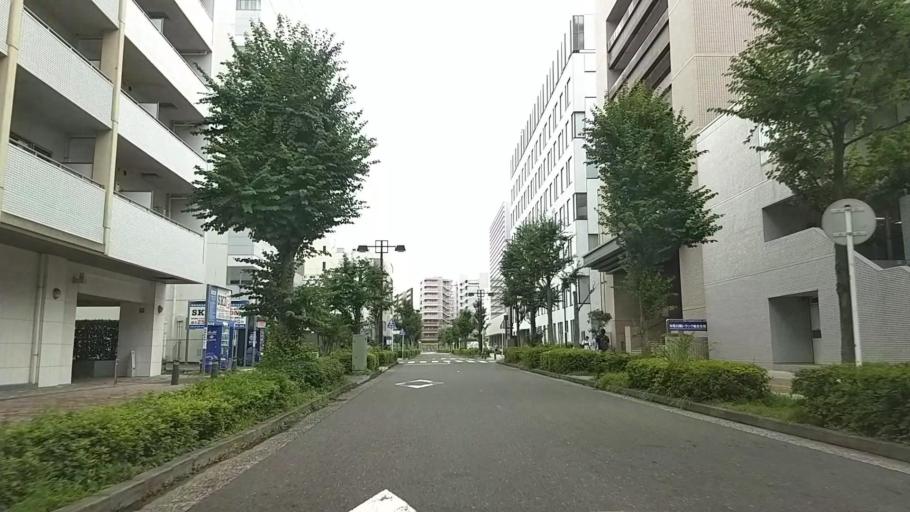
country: JP
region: Kanagawa
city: Yokohama
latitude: 35.5077
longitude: 139.6127
